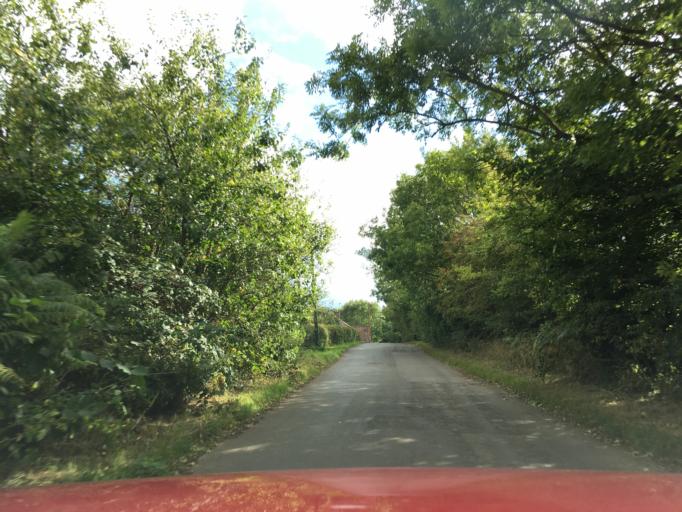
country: GB
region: England
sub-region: South Gloucestershire
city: Tytherington
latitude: 51.6078
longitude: -2.4738
